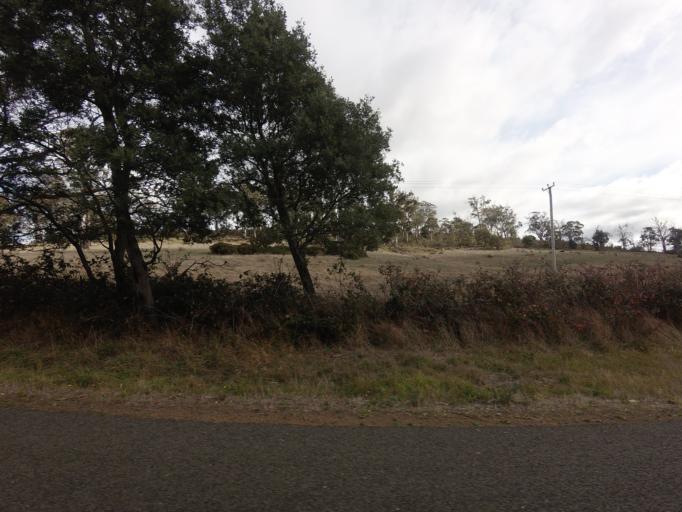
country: AU
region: Tasmania
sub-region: Brighton
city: Bridgewater
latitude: -42.4125
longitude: 147.4076
